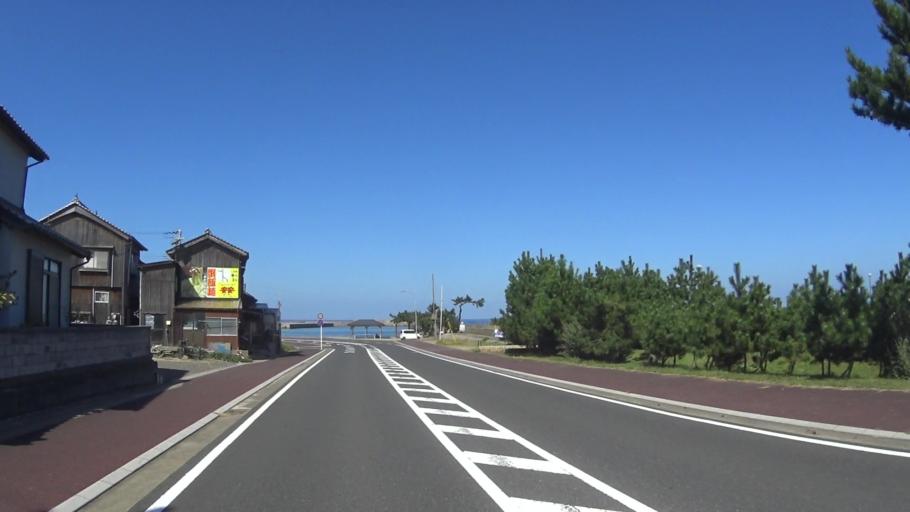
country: JP
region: Kyoto
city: Miyazu
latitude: 35.6905
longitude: 135.0188
